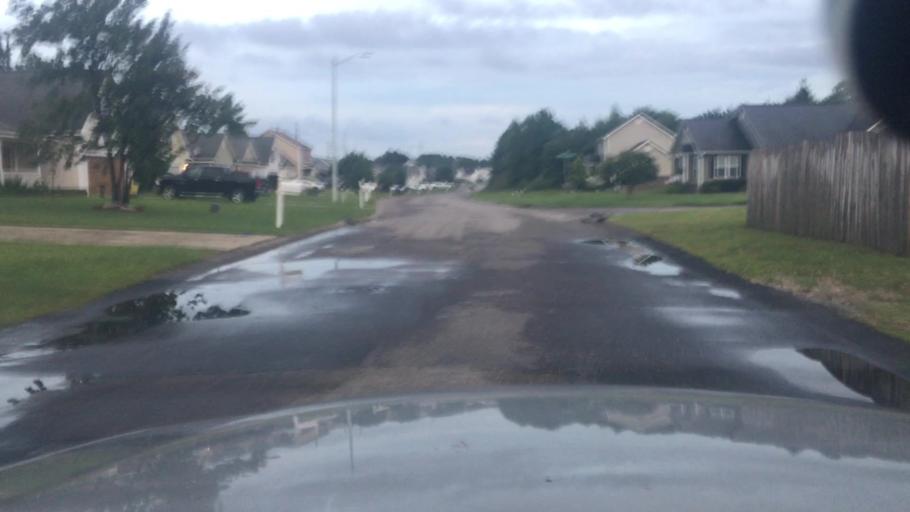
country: US
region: North Carolina
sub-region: Cumberland County
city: Hope Mills
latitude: 34.9855
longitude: -78.9202
